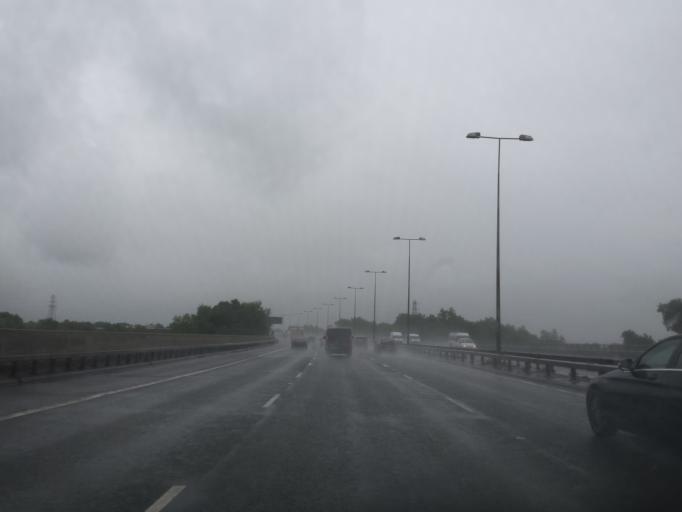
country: GB
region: England
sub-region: Derbyshire
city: Long Eaton
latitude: 52.8776
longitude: -1.3105
